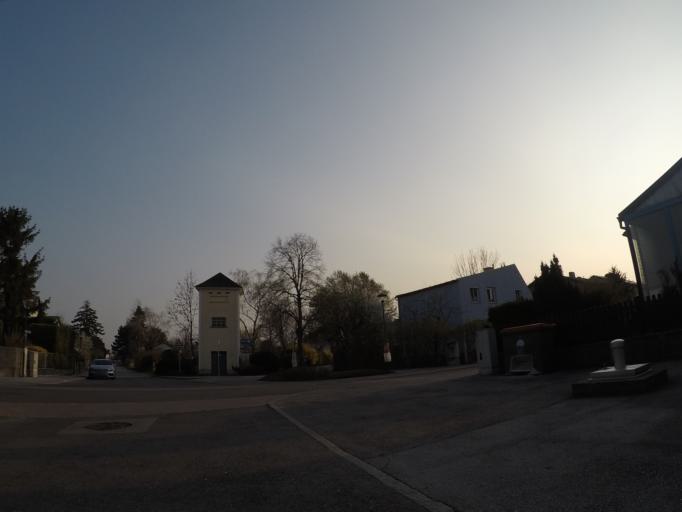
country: AT
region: Lower Austria
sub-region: Politischer Bezirk Modling
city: Wiener Neudorf
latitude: 48.0870
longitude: 16.3270
